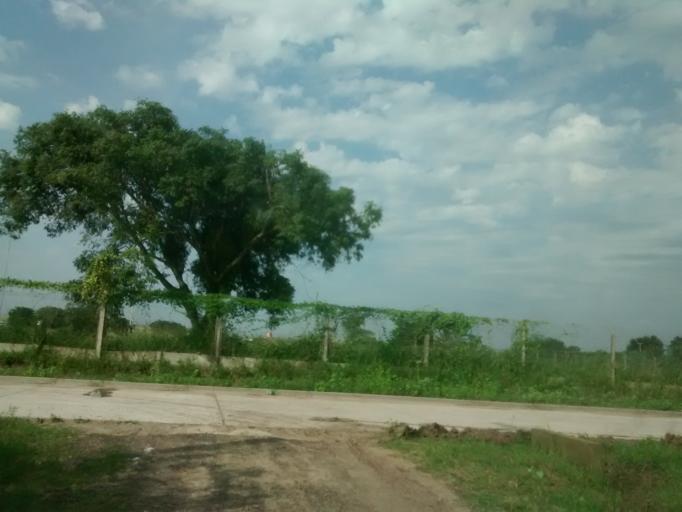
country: AR
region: Chaco
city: Fontana
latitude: -27.4044
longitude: -58.9817
